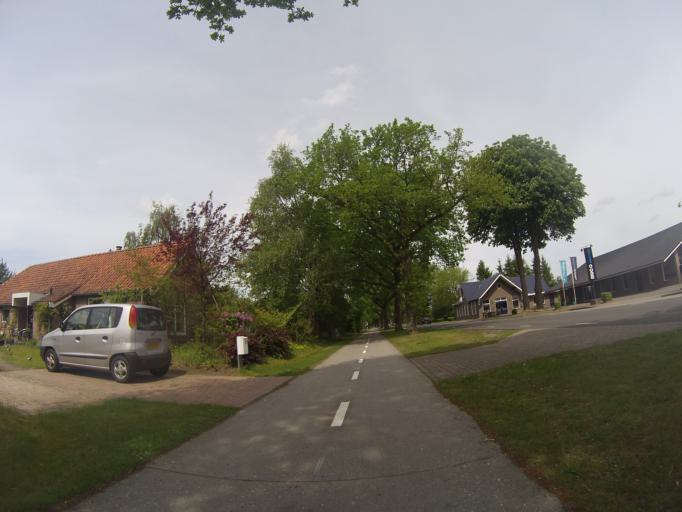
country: NL
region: Drenthe
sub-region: Gemeente Borger-Odoorn
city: Borger
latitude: 52.8568
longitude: 6.7500
